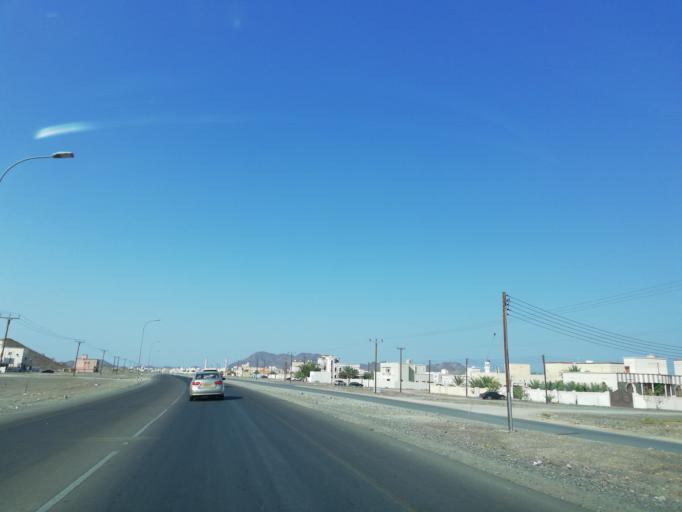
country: OM
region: Ash Sharqiyah
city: Ibra'
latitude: 22.7907
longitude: 58.1475
